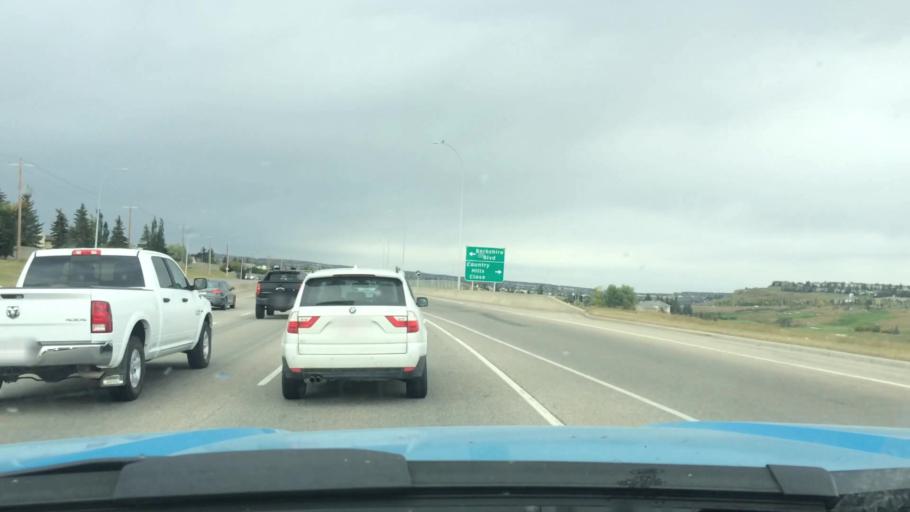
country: CA
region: Alberta
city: Calgary
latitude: 51.1352
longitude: -114.0784
